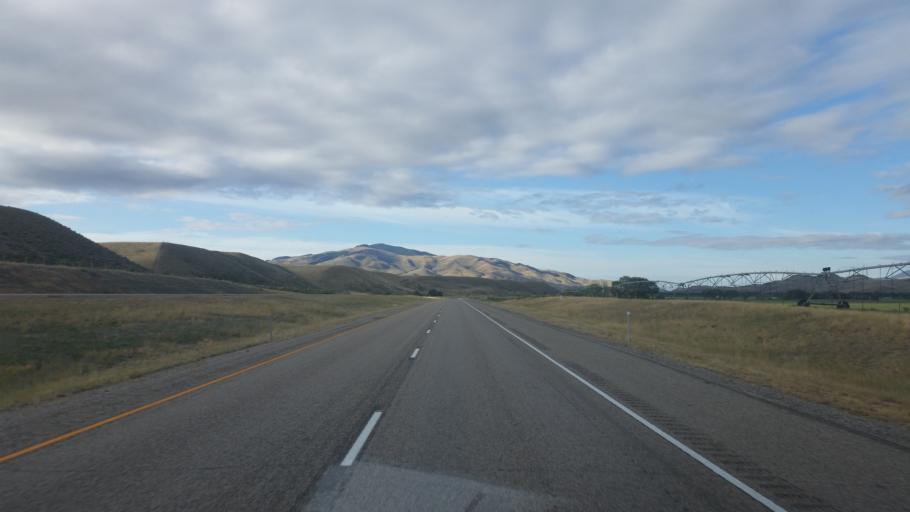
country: US
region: Montana
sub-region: Silver Bow County
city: Butte-Silver Bow (Balance)
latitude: 45.6571
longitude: -112.6767
